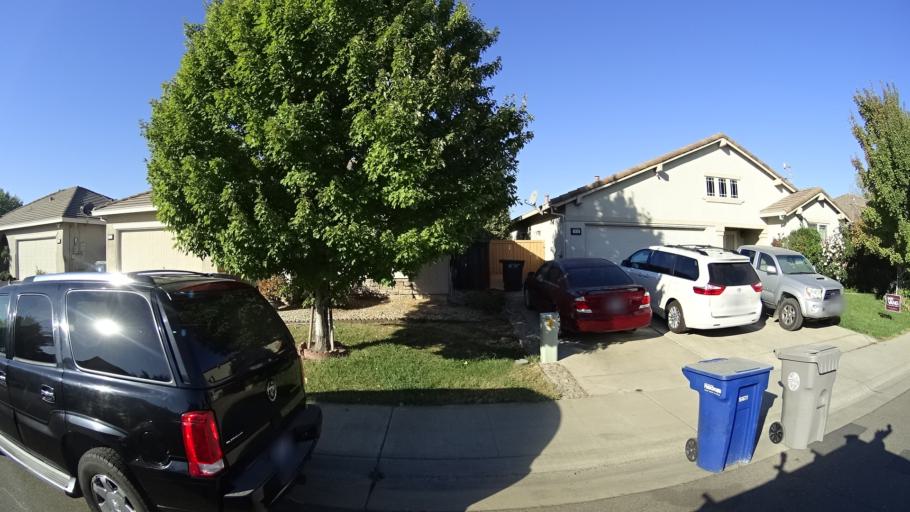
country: US
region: California
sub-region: Sacramento County
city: Parkway
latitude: 38.4729
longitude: -121.4934
